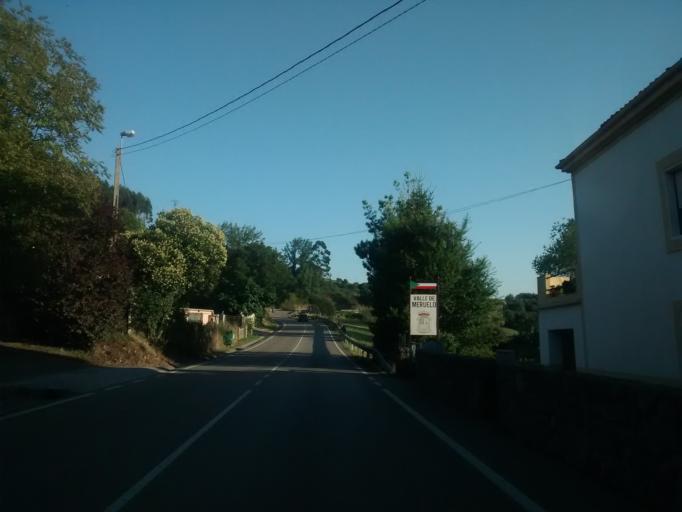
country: ES
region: Cantabria
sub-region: Provincia de Cantabria
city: San Miguel de Meruelo
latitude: 43.4653
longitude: -3.5856
